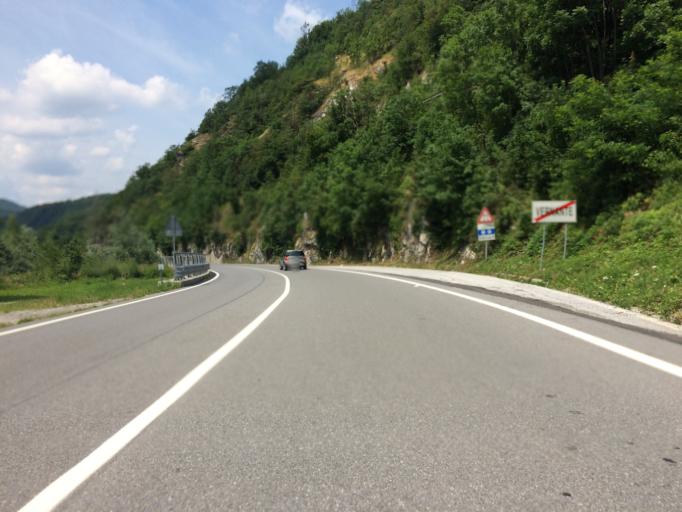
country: IT
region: Piedmont
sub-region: Provincia di Cuneo
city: Vernante
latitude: 44.2494
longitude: 7.5319
